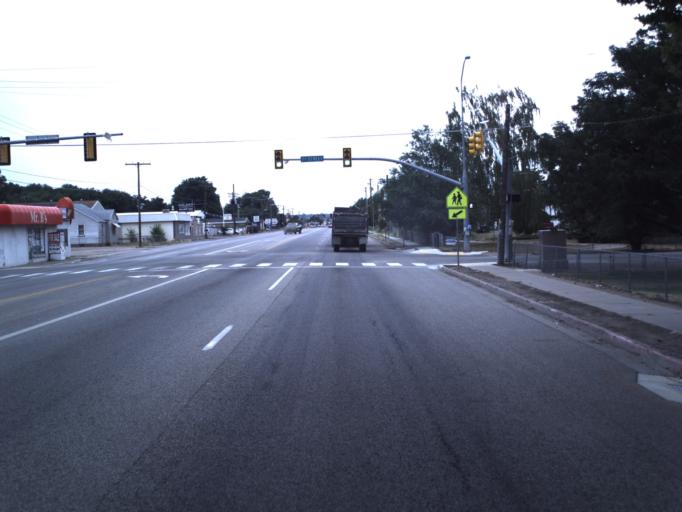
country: US
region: Utah
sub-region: Weber County
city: Ogden
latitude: 41.2523
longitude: -111.9781
